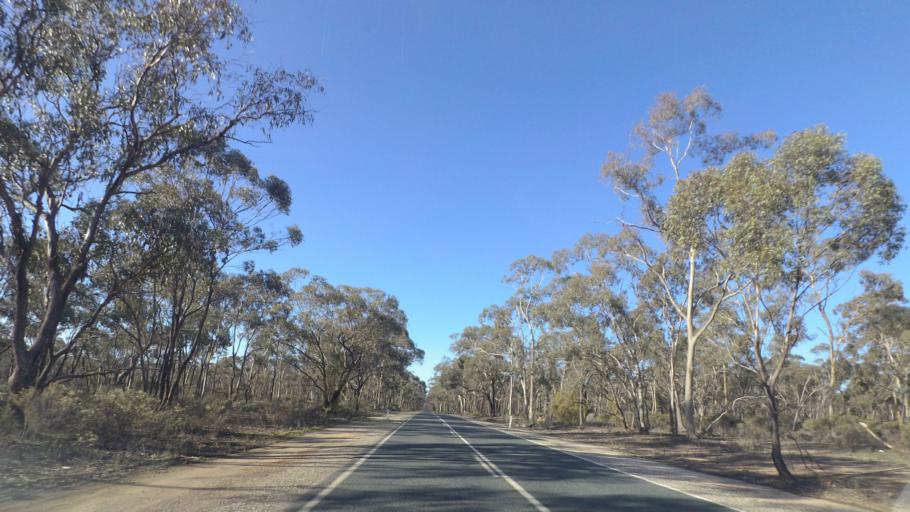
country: AU
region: Victoria
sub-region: Greater Bendigo
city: Epsom
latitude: -36.6730
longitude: 144.4055
